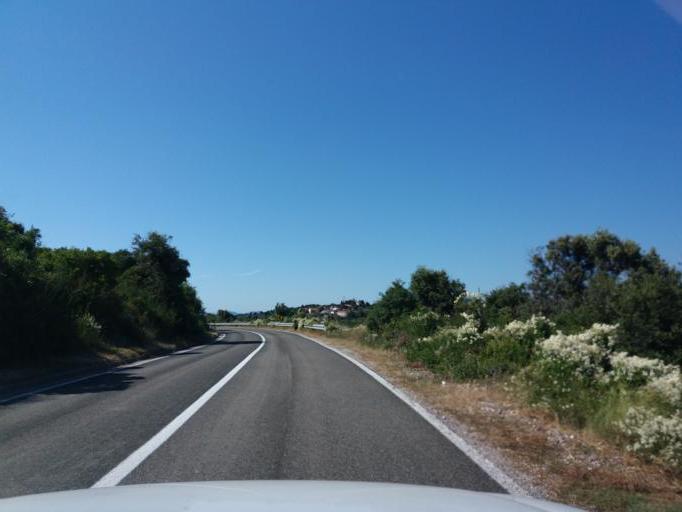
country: HR
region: Zadarska
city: Ugljan
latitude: 44.1052
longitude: 14.9387
